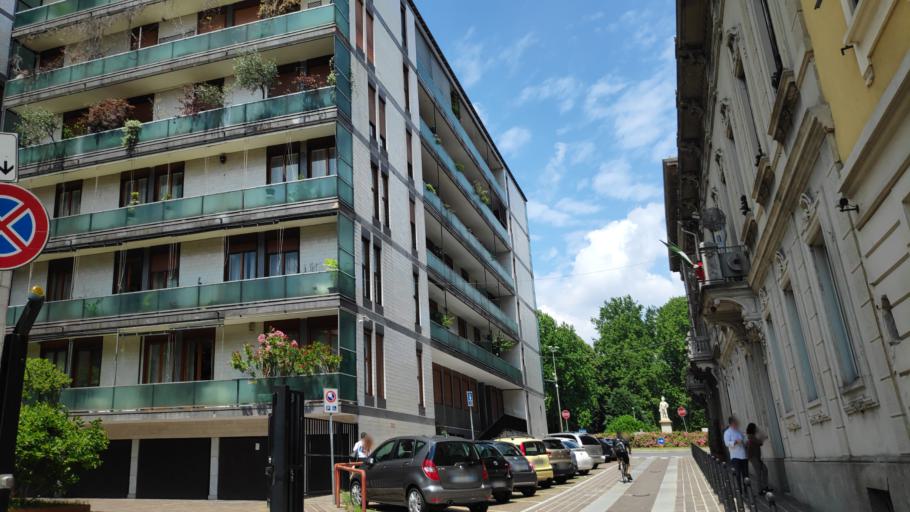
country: IT
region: Lombardy
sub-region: Provincia di Monza e Brianza
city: Monza
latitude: 45.5876
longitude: 9.2759
